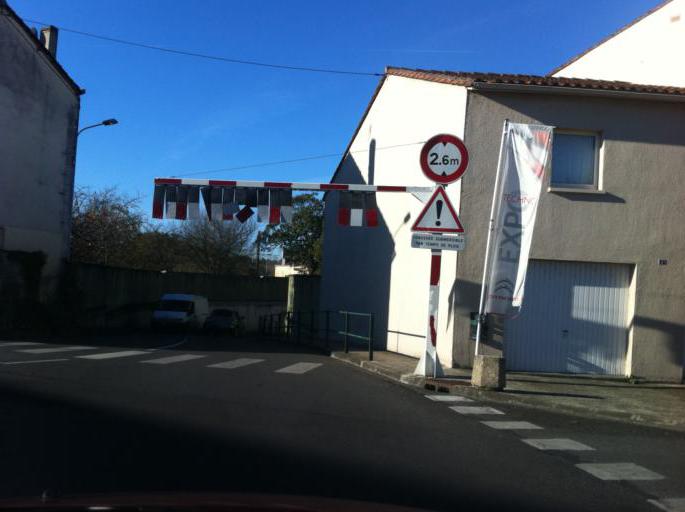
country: FR
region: Aquitaine
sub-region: Departement de la Dordogne
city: Saint-Aulaye
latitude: 45.2664
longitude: 0.1706
